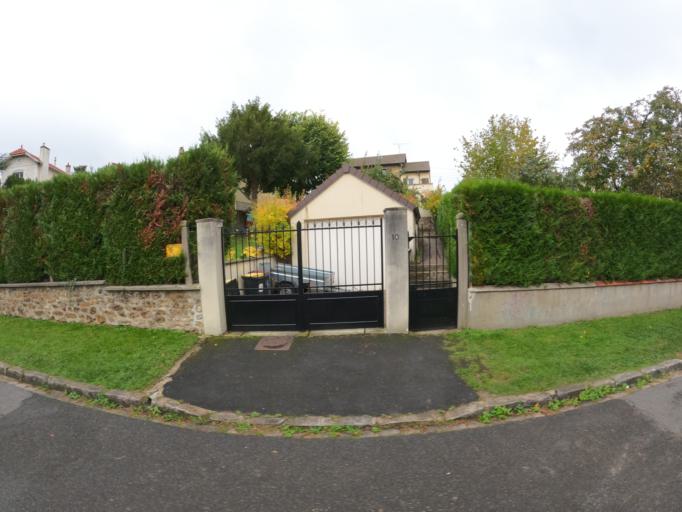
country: FR
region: Ile-de-France
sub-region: Departement du Val-de-Marne
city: Sucy-en-Brie
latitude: 48.7748
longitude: 2.5168
